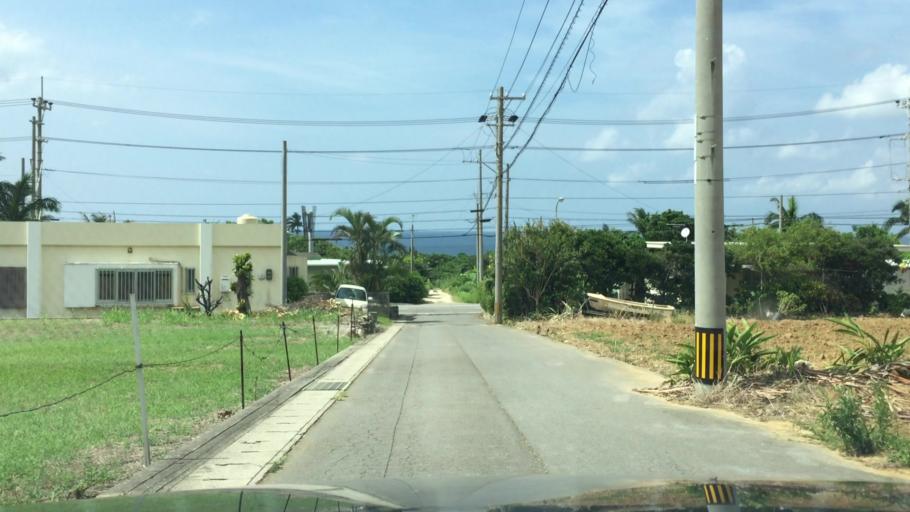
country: JP
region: Okinawa
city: Ishigaki
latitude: 24.4535
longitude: 124.1950
